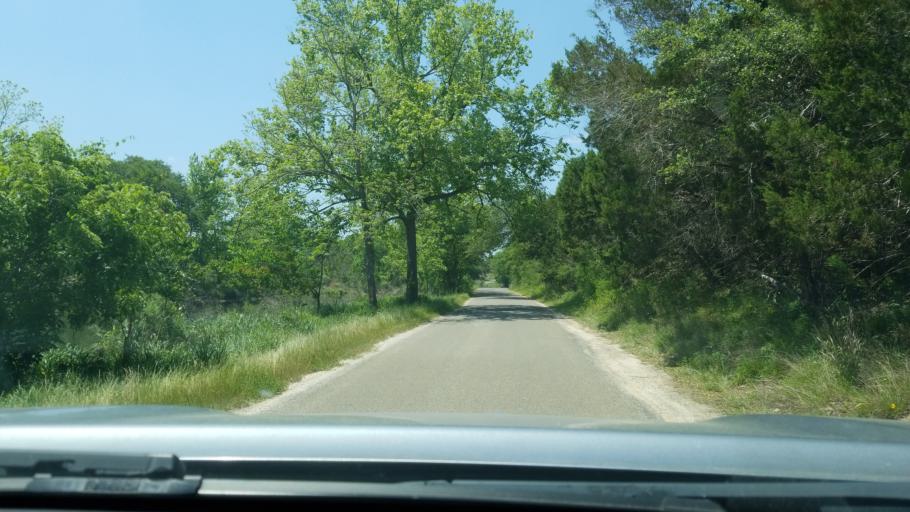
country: US
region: Texas
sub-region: Blanco County
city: Blanco
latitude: 29.9989
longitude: -98.4204
